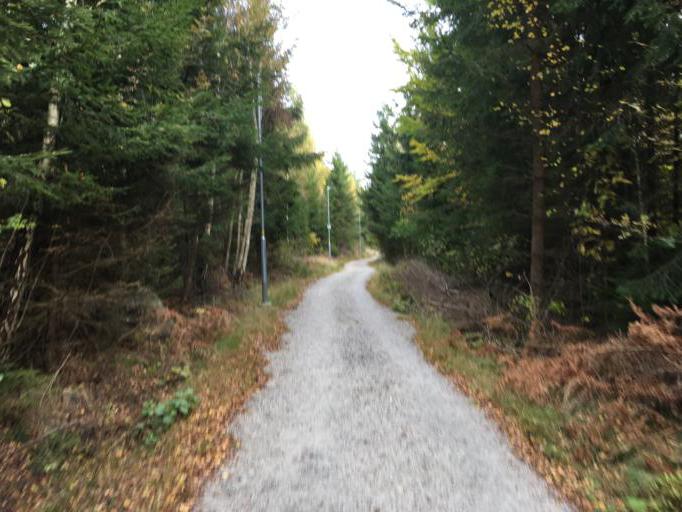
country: SE
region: Skane
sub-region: Hassleholms Kommun
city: Hassleholm
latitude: 56.1558
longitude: 13.7271
